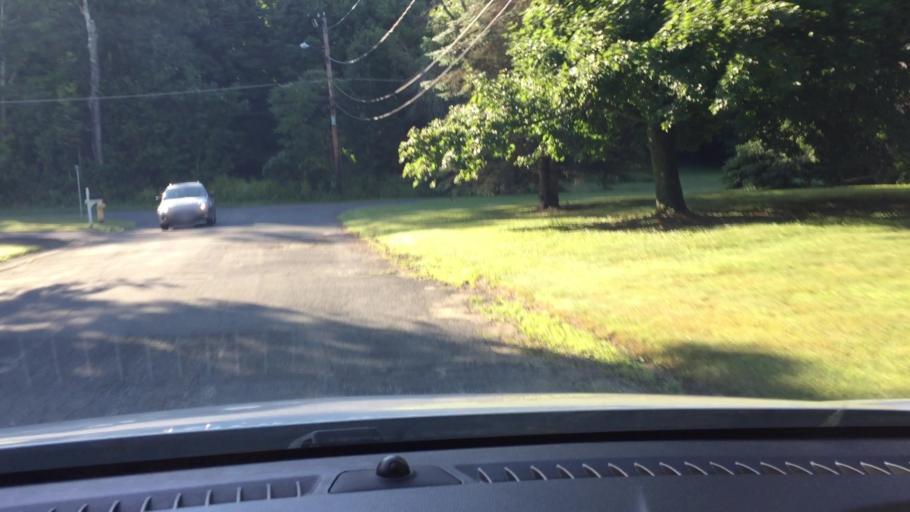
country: US
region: Massachusetts
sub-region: Berkshire County
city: Pittsfield
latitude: 42.4172
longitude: -73.2279
